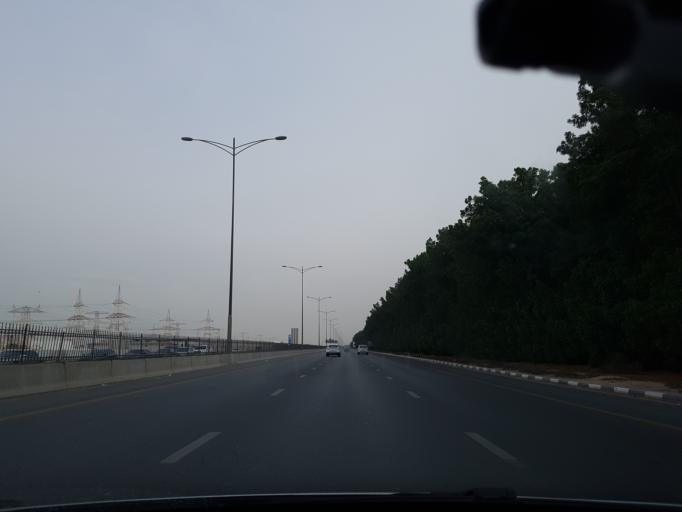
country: AE
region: Ajman
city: Ajman
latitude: 25.3699
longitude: 55.4609
